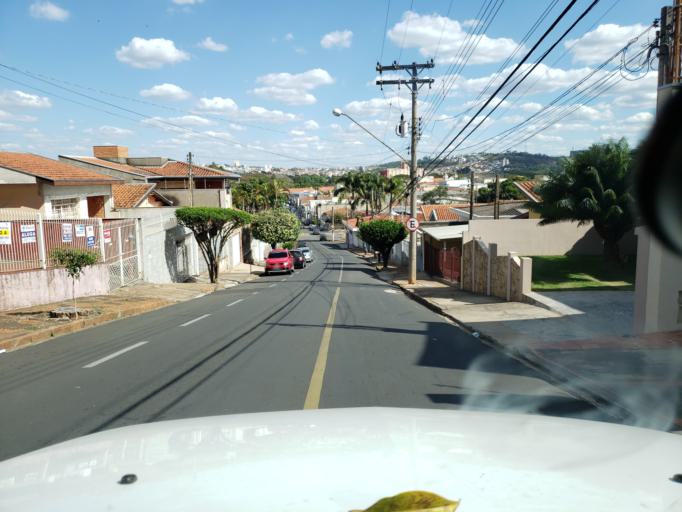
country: BR
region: Sao Paulo
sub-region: Moji-Guacu
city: Mogi-Gaucu
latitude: -22.3689
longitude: -46.9385
